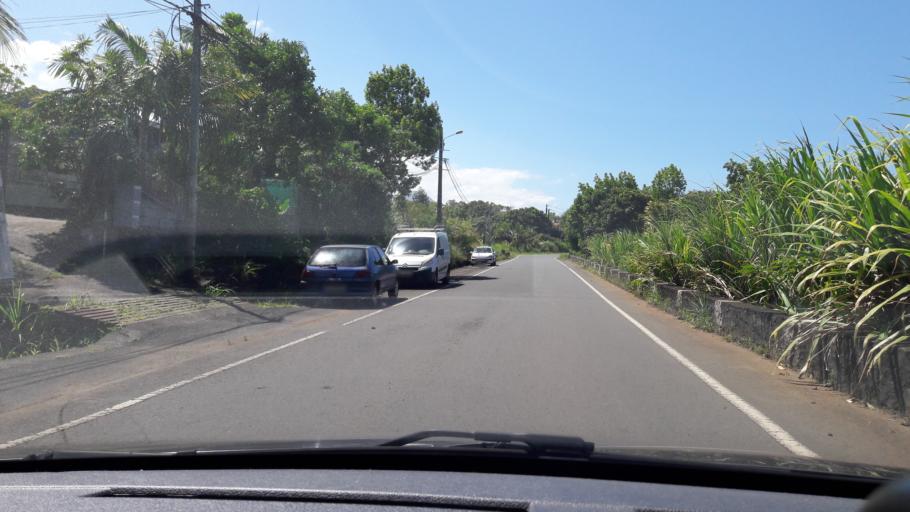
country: RE
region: Reunion
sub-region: Reunion
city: Saint-Benoit
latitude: -21.0899
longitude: 55.7015
